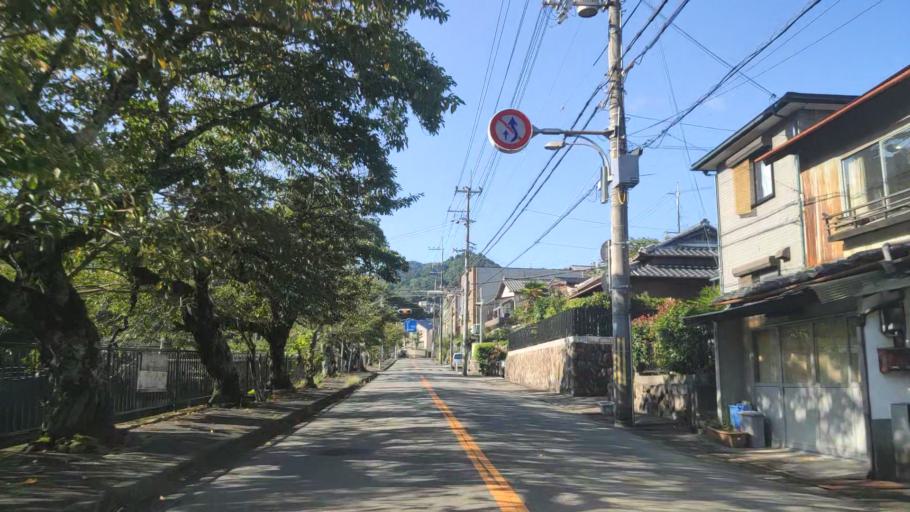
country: JP
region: Hyogo
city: Sandacho
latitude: 34.8043
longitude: 135.2494
